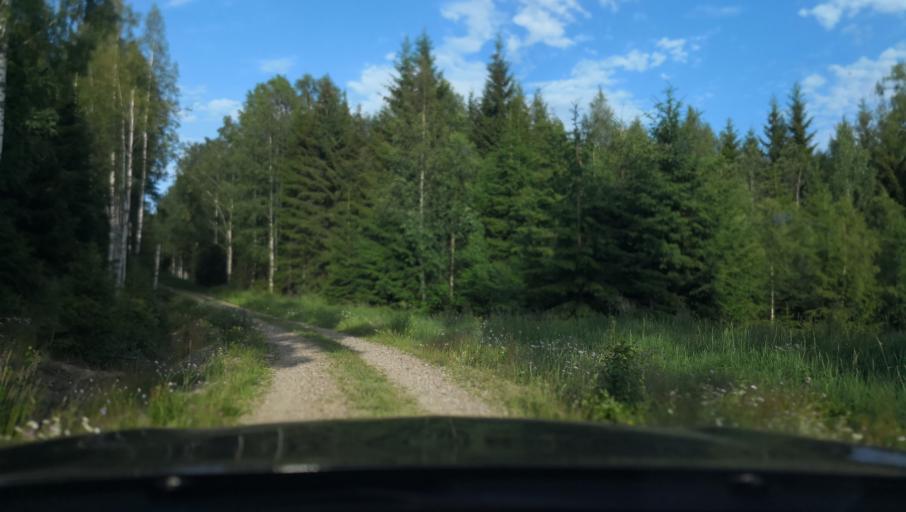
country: SE
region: Dalarna
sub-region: Ludvika Kommun
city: Ludvika
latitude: 60.0745
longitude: 15.2770
